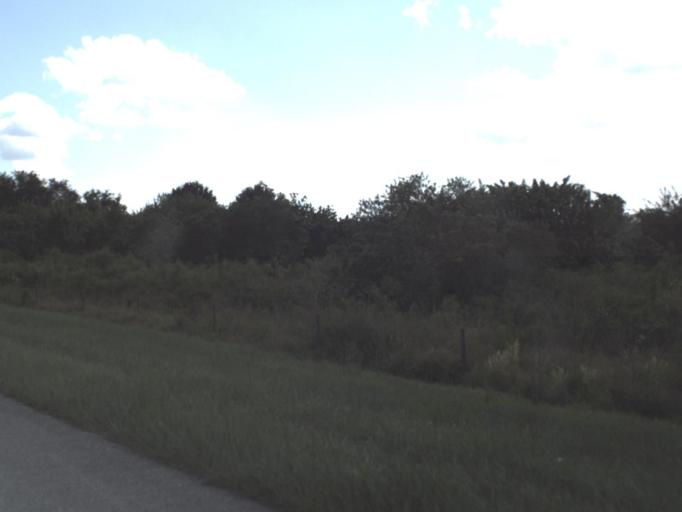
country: US
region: Florida
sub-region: Highlands County
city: Lake Placid
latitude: 27.3775
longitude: -81.0986
